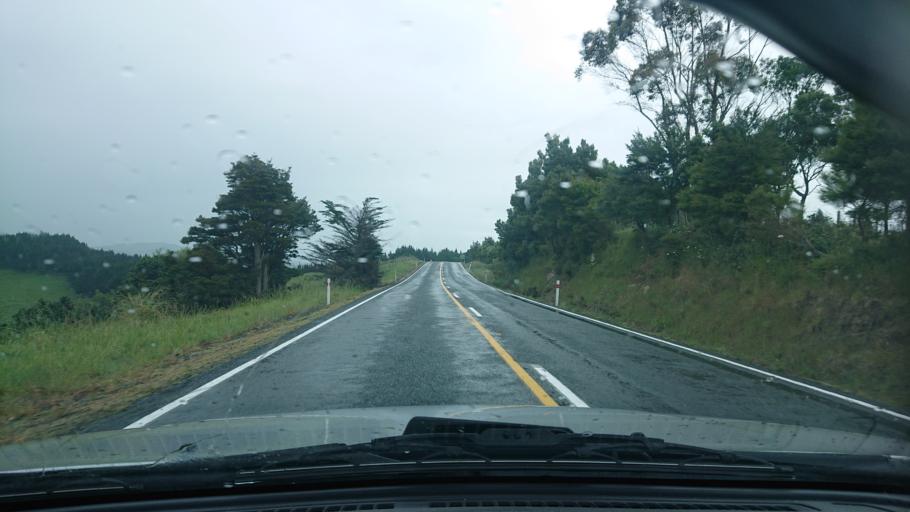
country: NZ
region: Auckland
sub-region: Auckland
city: Wellsford
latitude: -36.3567
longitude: 174.4696
